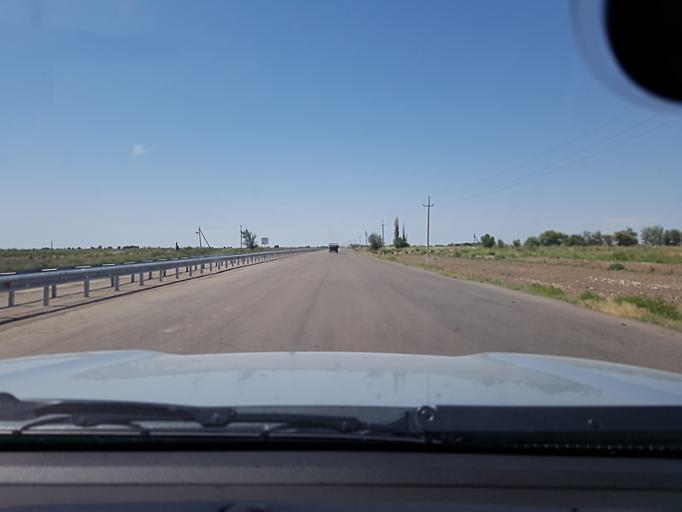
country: TM
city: Akdepe
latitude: 41.7369
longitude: 59.1304
